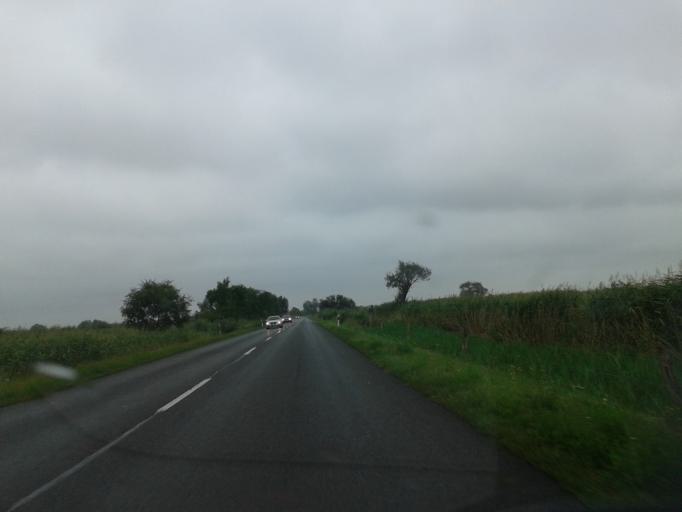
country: HU
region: Bacs-Kiskun
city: Akaszto
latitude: 46.7277
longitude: 19.1688
